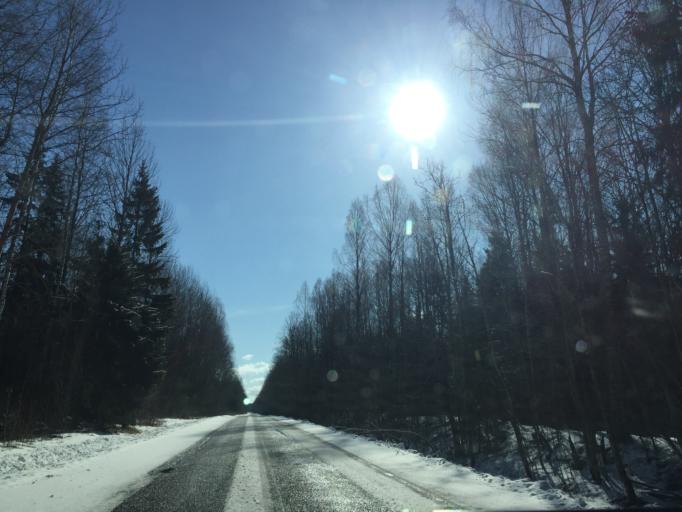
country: LV
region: Salacgrivas
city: Ainazi
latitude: 58.0047
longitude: 24.5087
